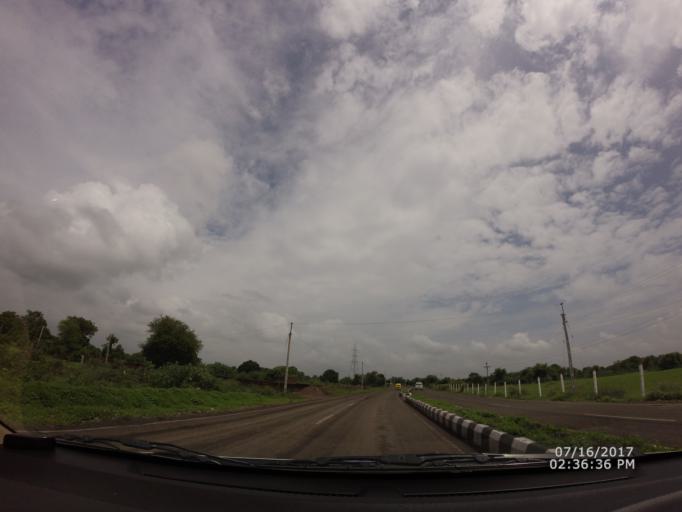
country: IN
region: Gujarat
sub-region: Ahmadabad
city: Sanand
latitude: 23.1193
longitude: 72.3887
